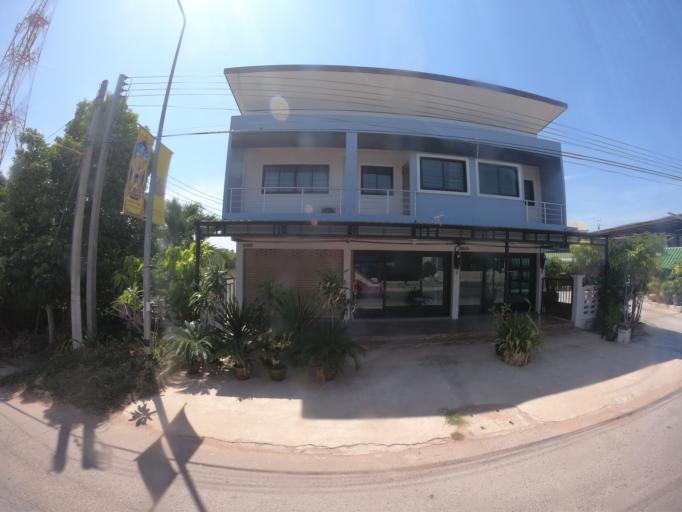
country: TH
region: Khon Kaen
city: Ban Phai
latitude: 16.0670
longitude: 102.7217
